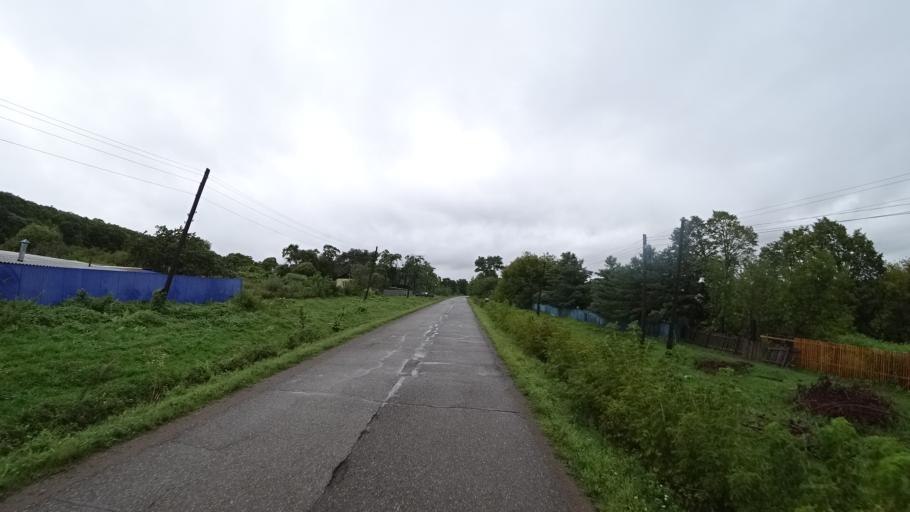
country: RU
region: Primorskiy
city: Monastyrishche
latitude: 44.2660
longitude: 132.4204
